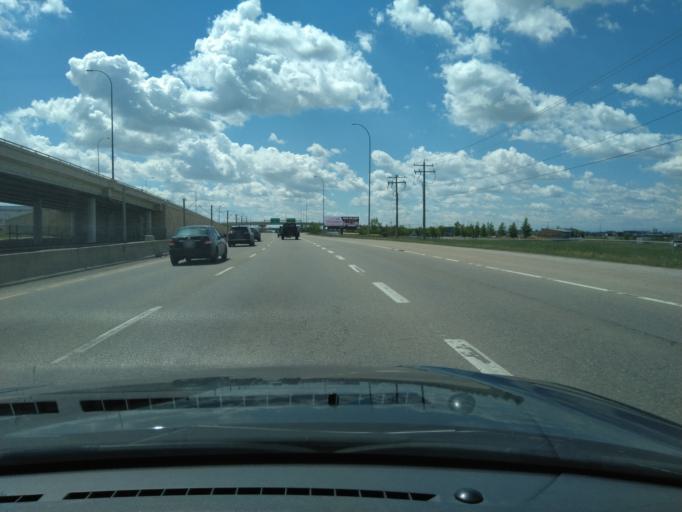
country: CA
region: Alberta
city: Calgary
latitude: 51.1024
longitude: -113.9820
